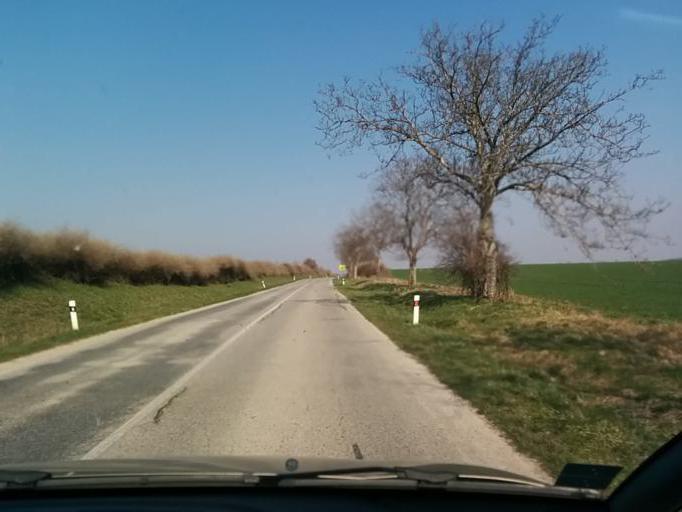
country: SK
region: Trnavsky
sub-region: Okres Galanta
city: Galanta
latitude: 48.2932
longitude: 17.7653
